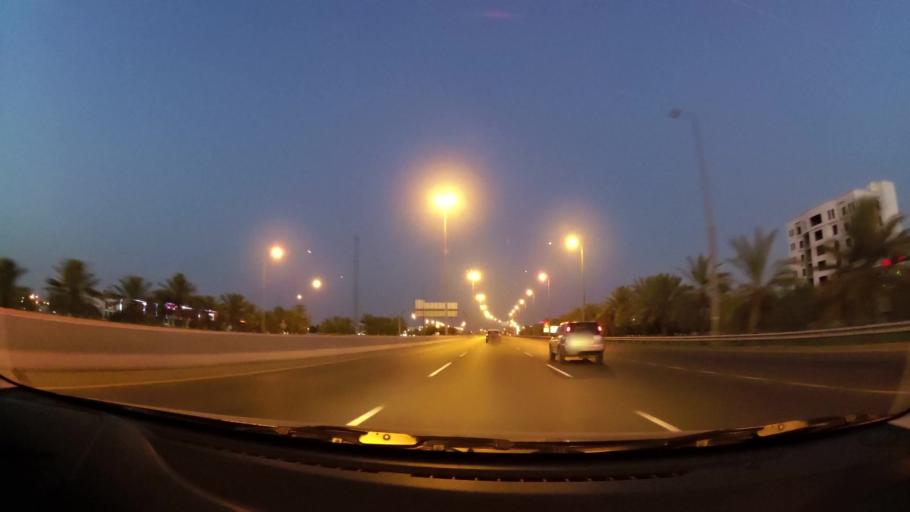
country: OM
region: Muhafazat Masqat
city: As Sib al Jadidah
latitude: 23.6567
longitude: 58.1974
